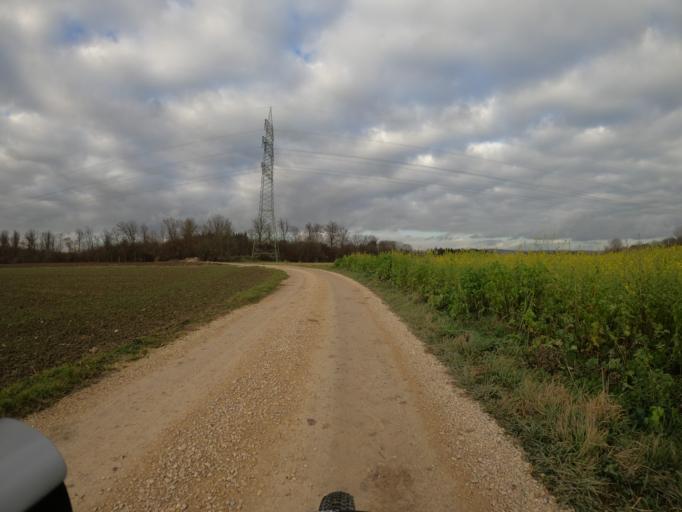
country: DE
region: Baden-Wuerttemberg
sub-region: Regierungsbezirk Stuttgart
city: Notzingen
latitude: 48.6799
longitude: 9.4511
